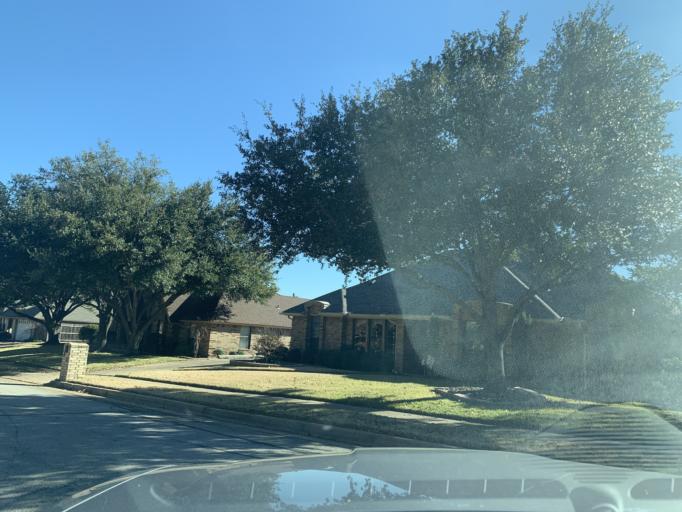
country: US
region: Texas
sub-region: Tarrant County
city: Bedford
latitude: 32.8485
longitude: -97.1559
